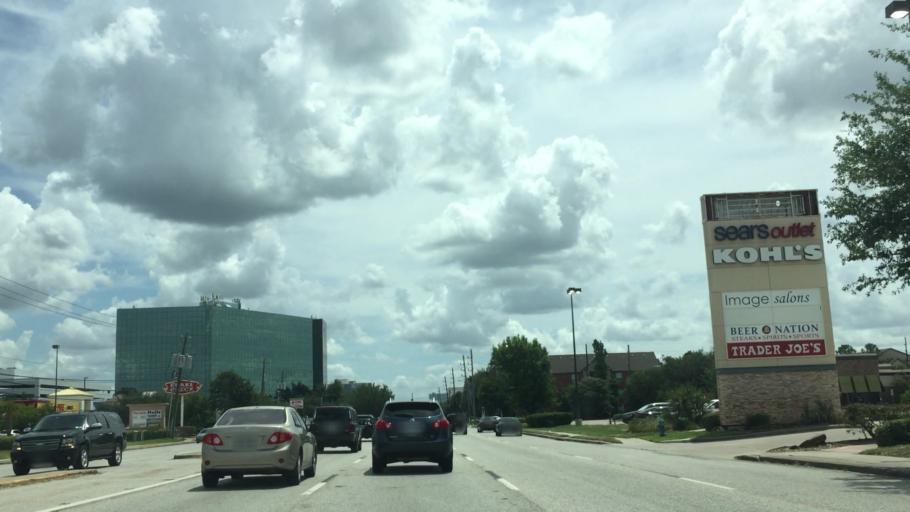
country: US
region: Texas
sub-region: Harris County
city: Bunker Hill Village
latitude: 29.7357
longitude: -95.5831
